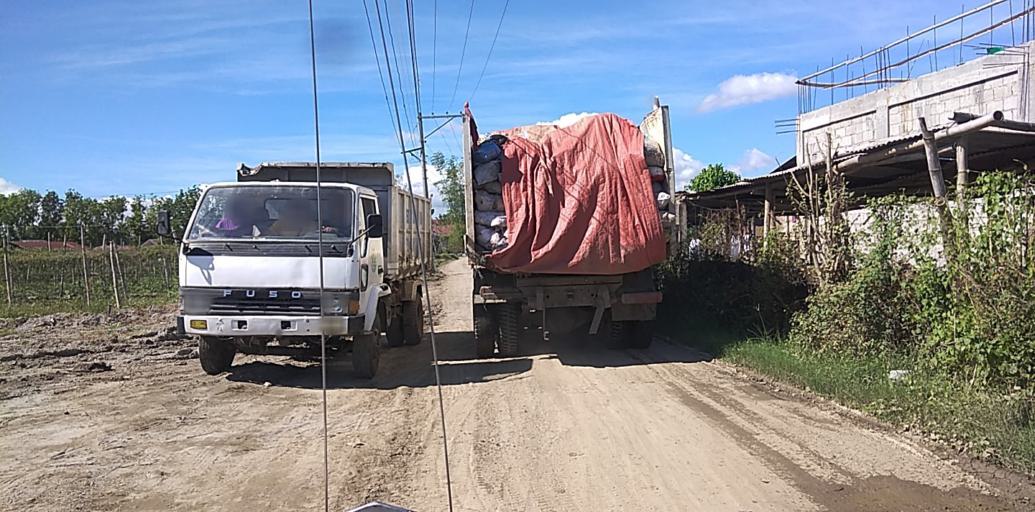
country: PH
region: Central Luzon
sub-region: Province of Pampanga
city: Candating
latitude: 15.1286
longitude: 120.8087
